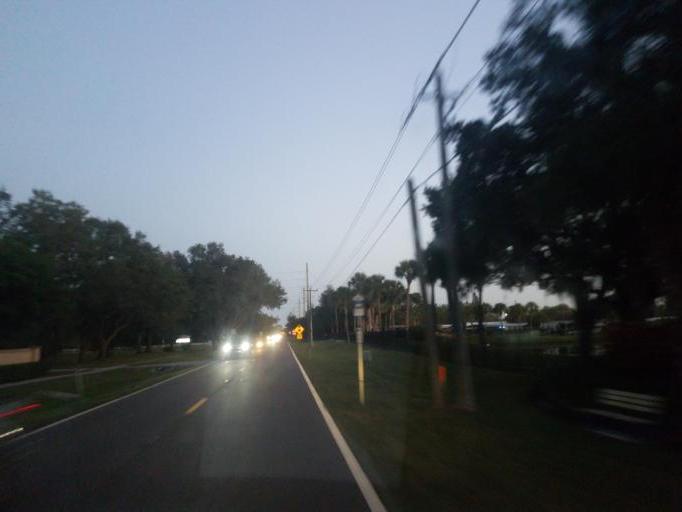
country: US
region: Florida
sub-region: Sarasota County
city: Lake Sarasota
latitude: 27.2752
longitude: -82.4564
